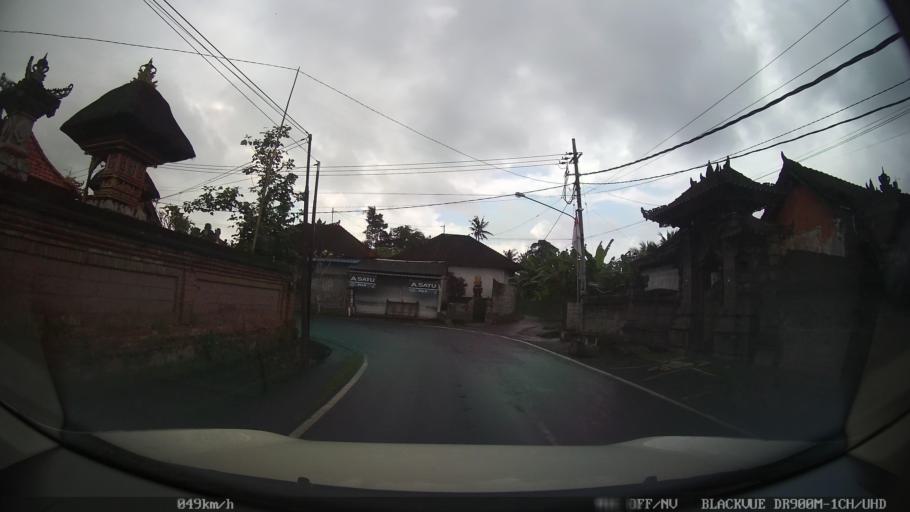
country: ID
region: Bali
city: Banjar Pande
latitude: -8.5231
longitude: 115.2286
